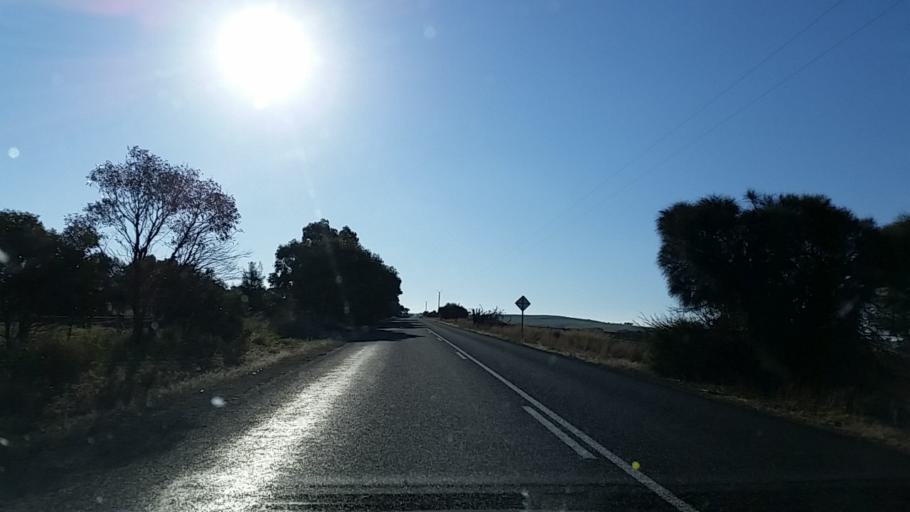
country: AU
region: South Australia
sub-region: Alexandrina
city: Strathalbyn
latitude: -35.1949
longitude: 138.9626
